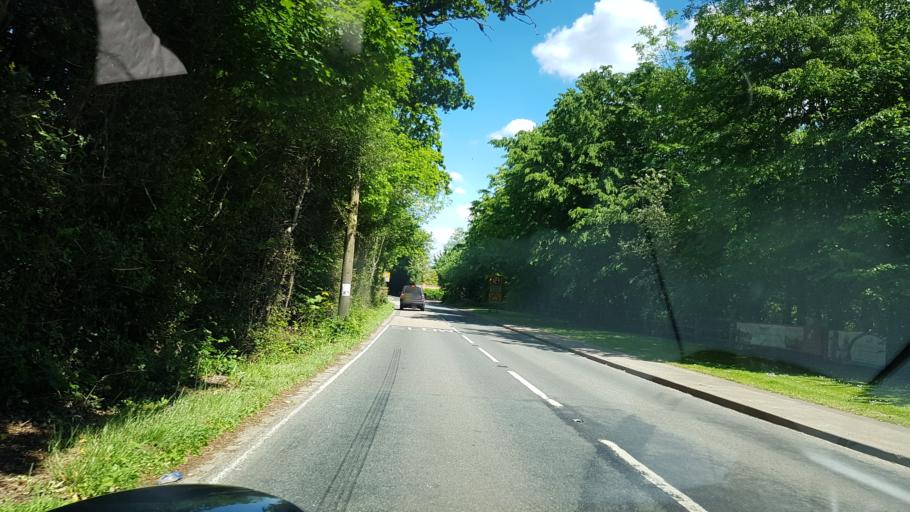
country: GB
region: England
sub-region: Surrey
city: Cranleigh
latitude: 51.1405
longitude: -0.5183
